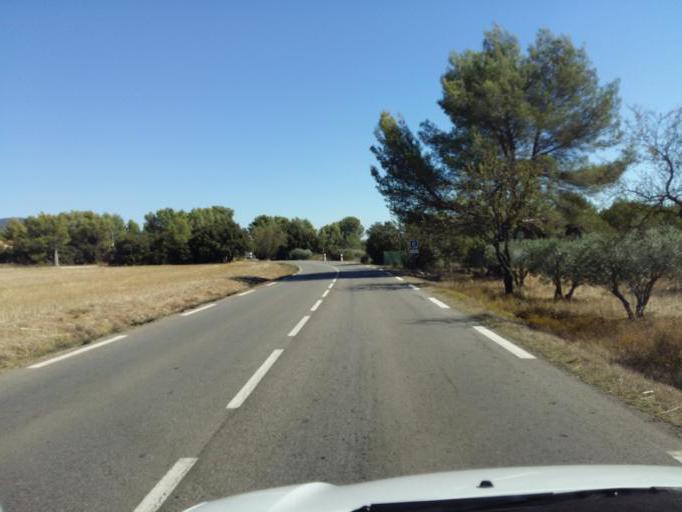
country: FR
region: Provence-Alpes-Cote d'Azur
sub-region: Departement du Vaucluse
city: Merindol
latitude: 43.7523
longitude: 5.2140
